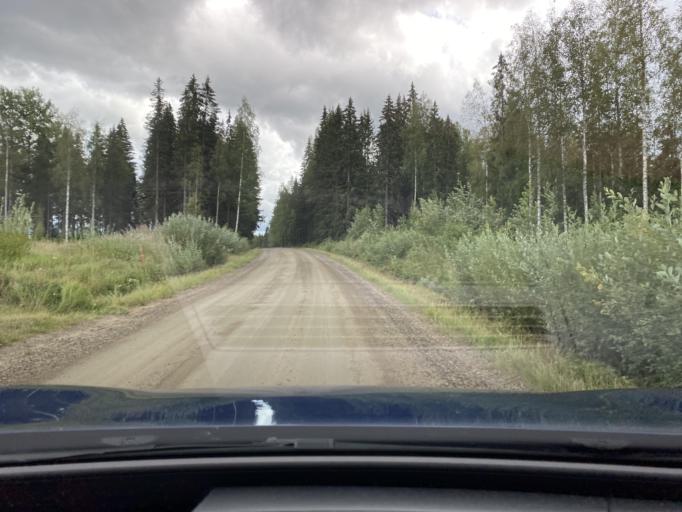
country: FI
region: Pirkanmaa
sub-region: Lounais-Pirkanmaa
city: Punkalaidun
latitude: 61.2284
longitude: 23.1524
